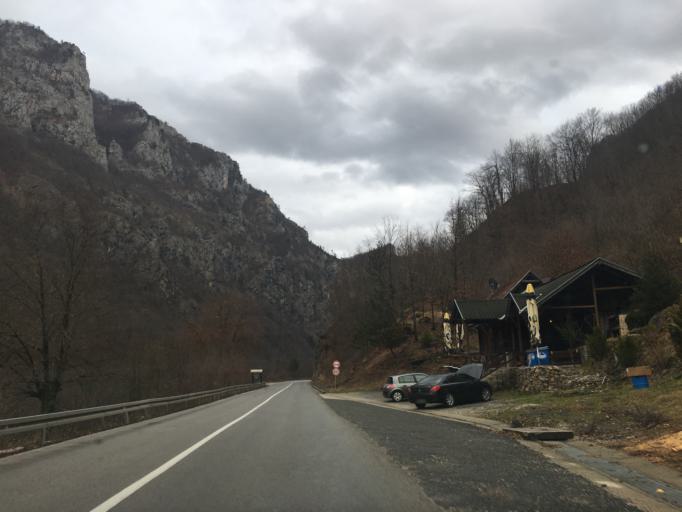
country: RS
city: Sokolovo Brdo
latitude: 43.1820
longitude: 19.7630
